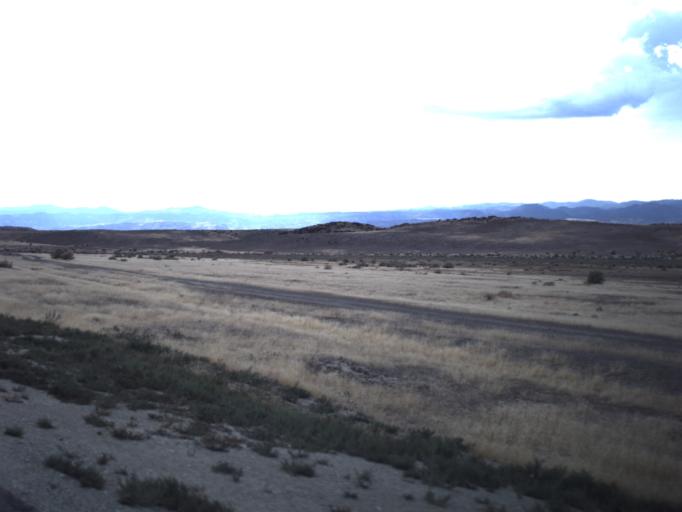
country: US
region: Utah
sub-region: Sevier County
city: Richfield
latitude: 38.7734
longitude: -111.9584
